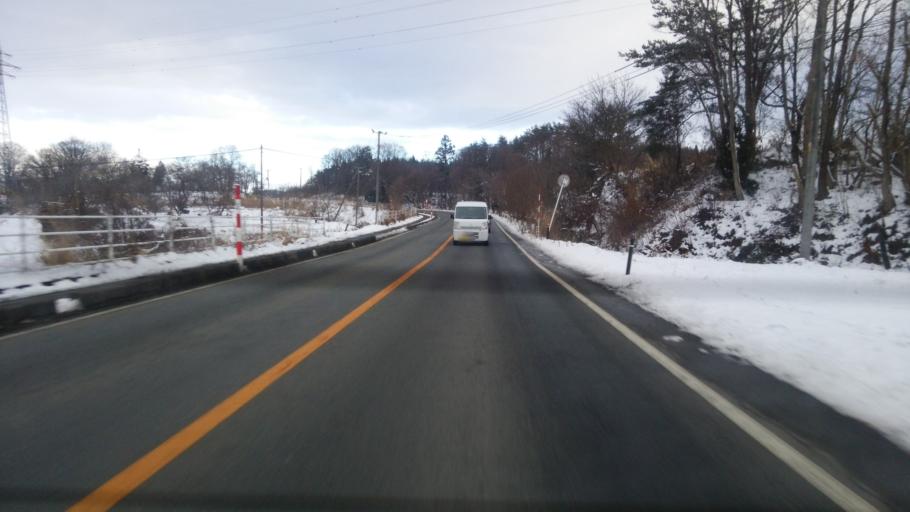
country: JP
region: Fukushima
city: Kitakata
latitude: 37.5626
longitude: 139.9721
